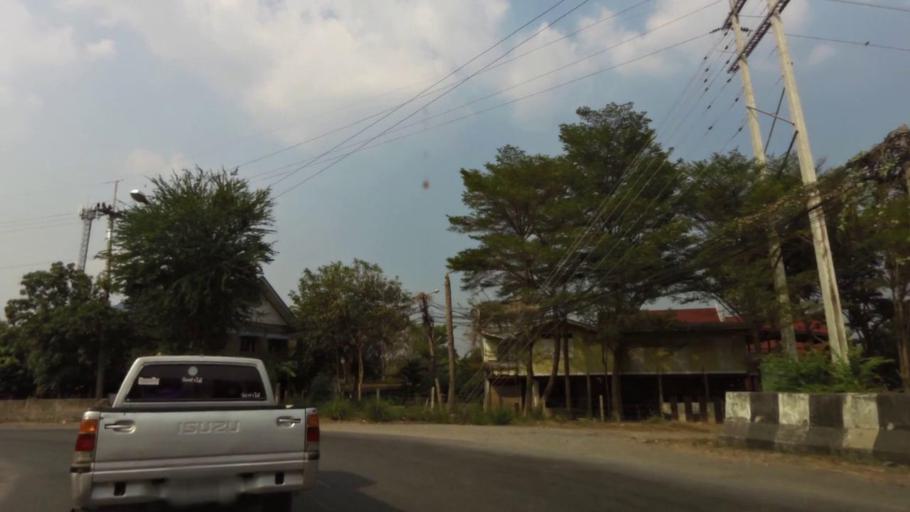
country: TH
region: Phra Nakhon Si Ayutthaya
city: Phra Nakhon Si Ayutthaya
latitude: 14.3048
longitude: 100.5647
